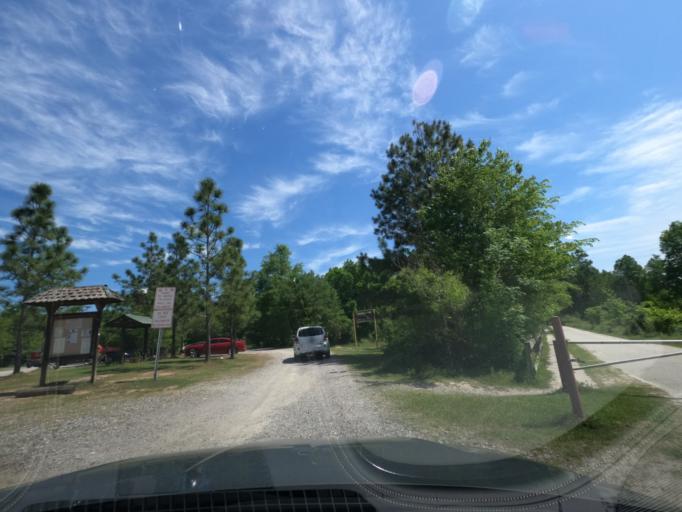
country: US
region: Georgia
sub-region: Richmond County
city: Augusta
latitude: 33.3845
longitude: -81.9677
